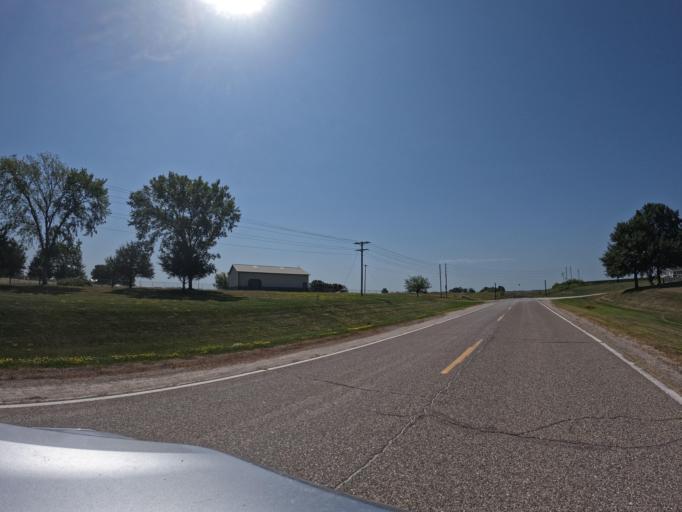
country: US
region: Iowa
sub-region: Henry County
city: Mount Pleasant
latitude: 40.9310
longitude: -91.5403
